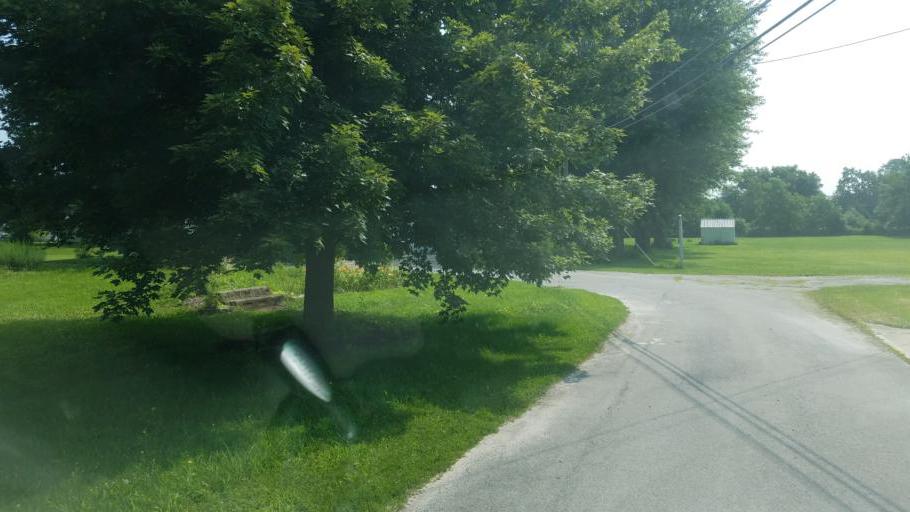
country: US
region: Ohio
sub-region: Union County
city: Richwood
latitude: 40.5788
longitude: -83.3833
